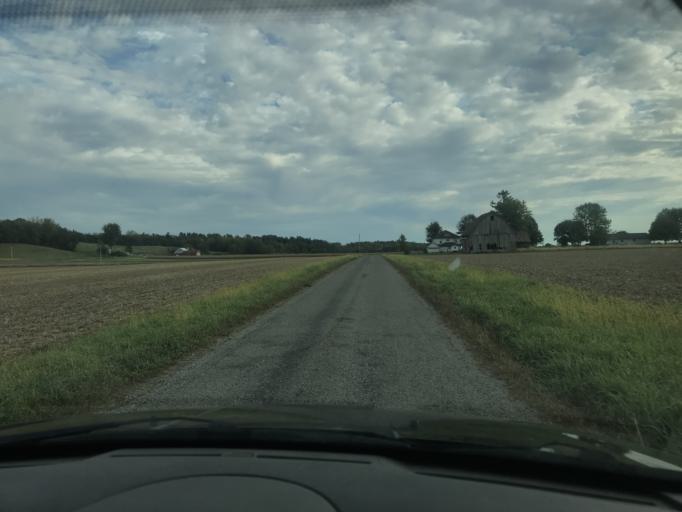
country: US
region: Ohio
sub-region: Logan County
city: West Liberty
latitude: 40.2357
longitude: -83.6852
